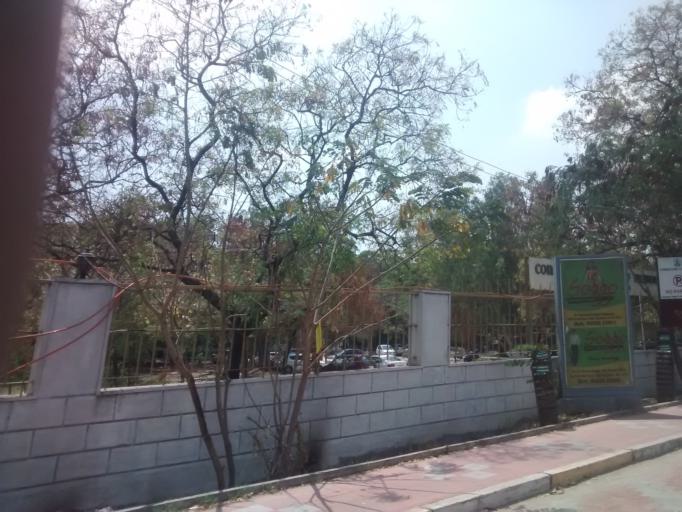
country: IN
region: Tamil Nadu
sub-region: Coimbatore
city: Singanallur
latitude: 11.0294
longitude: 77.0267
